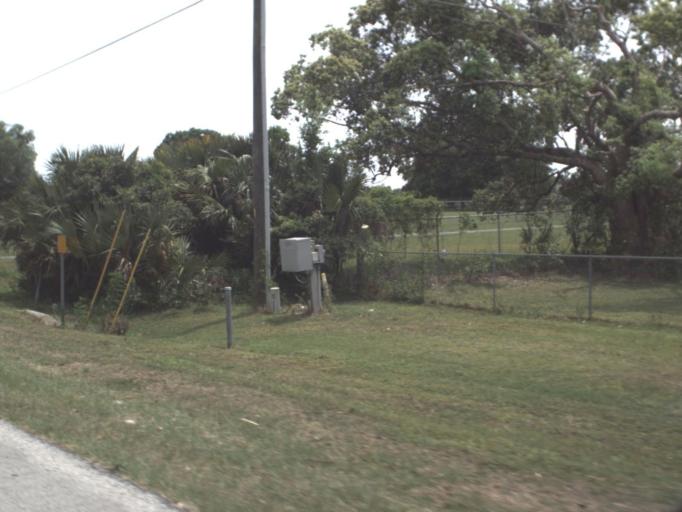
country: US
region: Florida
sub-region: Lake County
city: Mount Dora
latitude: 28.8516
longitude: -81.6238
